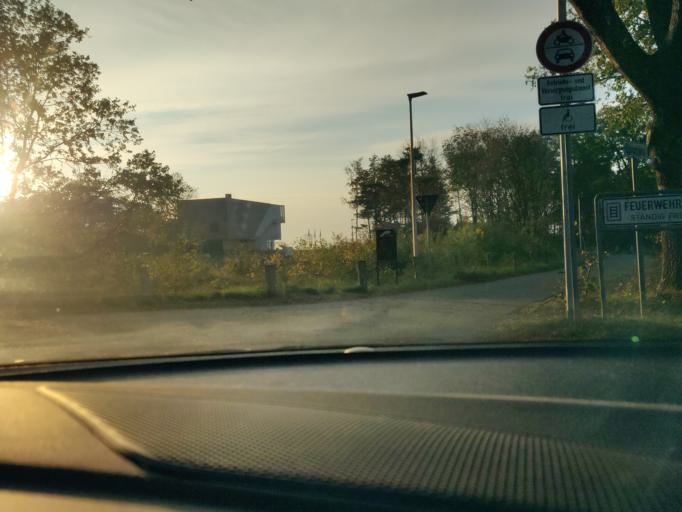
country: DE
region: Lower Saxony
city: Nordholz
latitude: 53.8645
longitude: 8.6008
